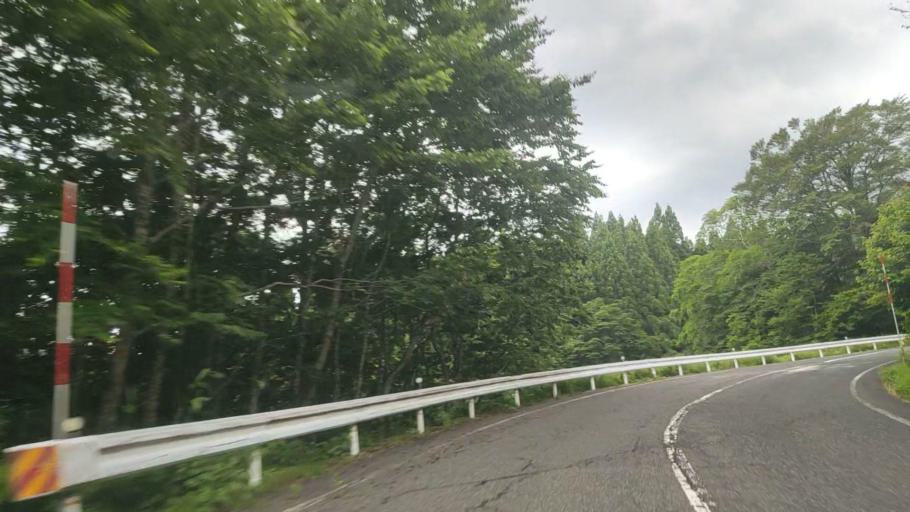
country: JP
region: Tottori
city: Kurayoshi
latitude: 35.3150
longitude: 134.0036
